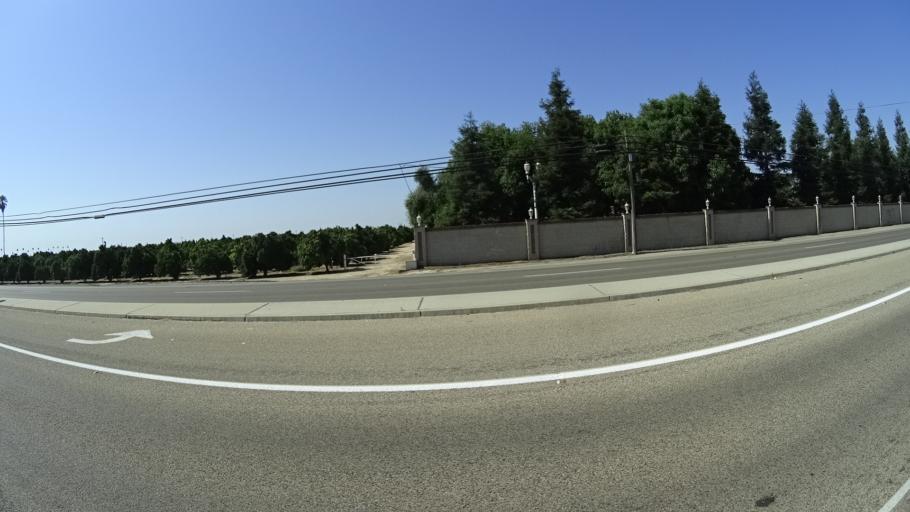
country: US
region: California
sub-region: Fresno County
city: Sunnyside
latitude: 36.7078
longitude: -119.7083
